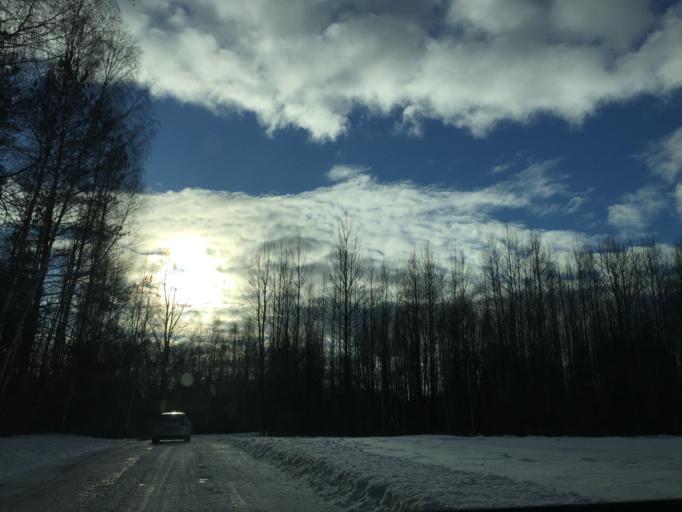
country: LV
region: Lielvarde
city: Lielvarde
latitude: 56.5726
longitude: 24.7995
